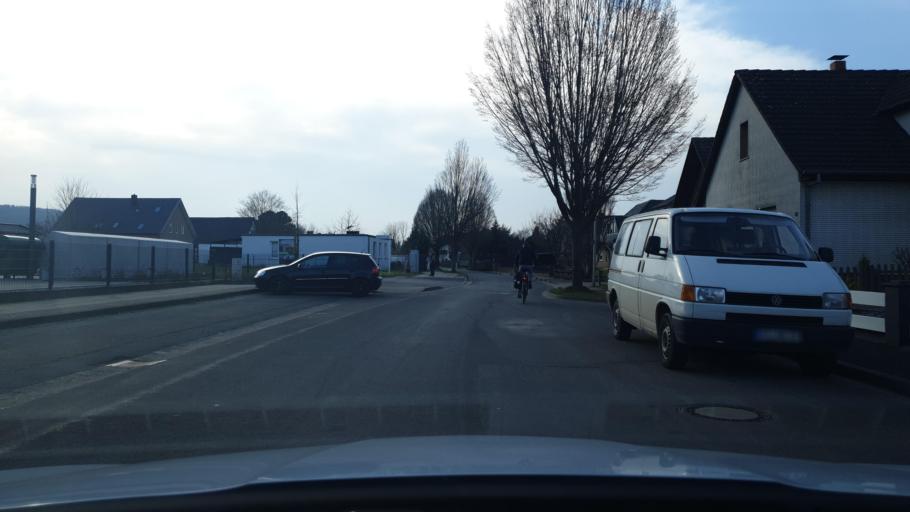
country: DE
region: North Rhine-Westphalia
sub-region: Regierungsbezirk Detmold
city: Minden
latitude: 52.2709
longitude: 8.8586
